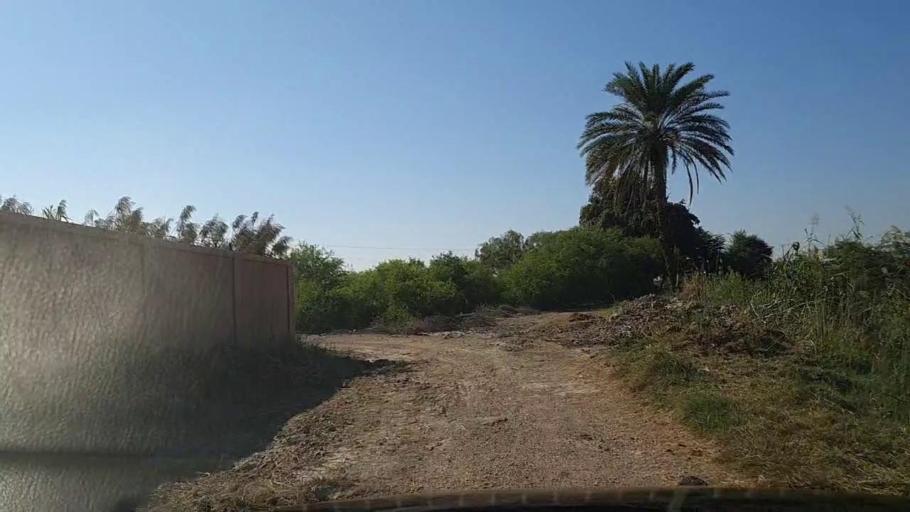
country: PK
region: Sindh
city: Thatta
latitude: 24.7014
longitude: 67.9040
